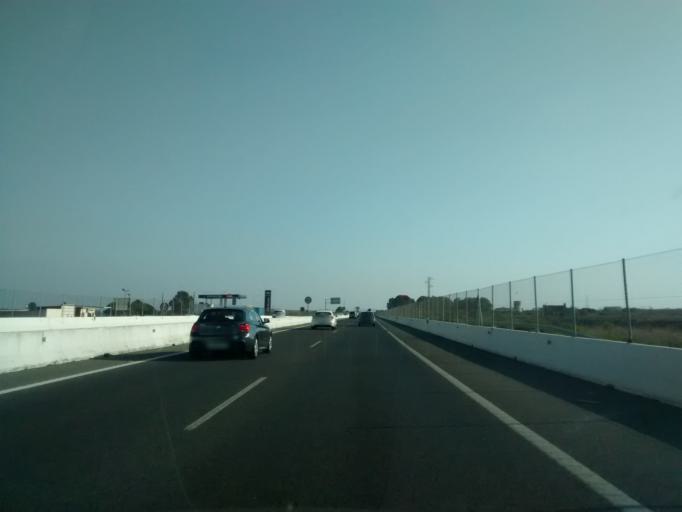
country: ES
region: Andalusia
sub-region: Provincia de Cadiz
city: San Fernando
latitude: 36.4906
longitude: -6.1437
